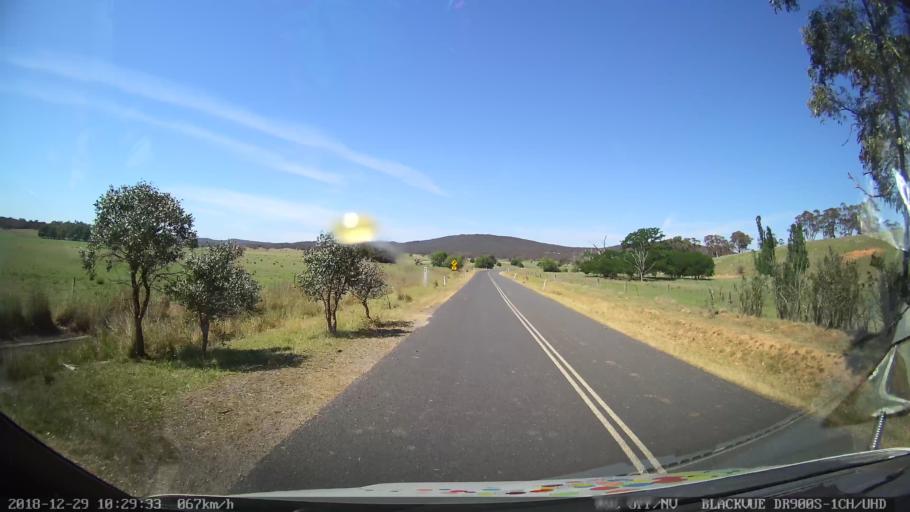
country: AU
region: New South Wales
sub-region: Yass Valley
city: Gundaroo
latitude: -34.9530
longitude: 149.4575
